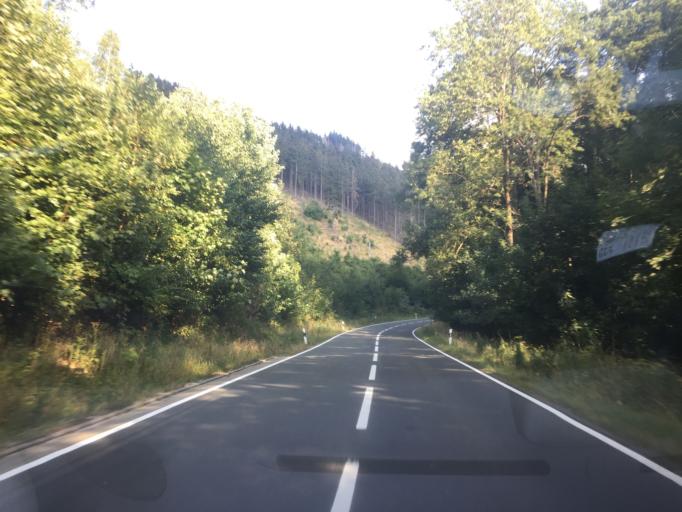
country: DE
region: Saxony-Anhalt
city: Darlingerode
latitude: 51.8014
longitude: 10.7329
